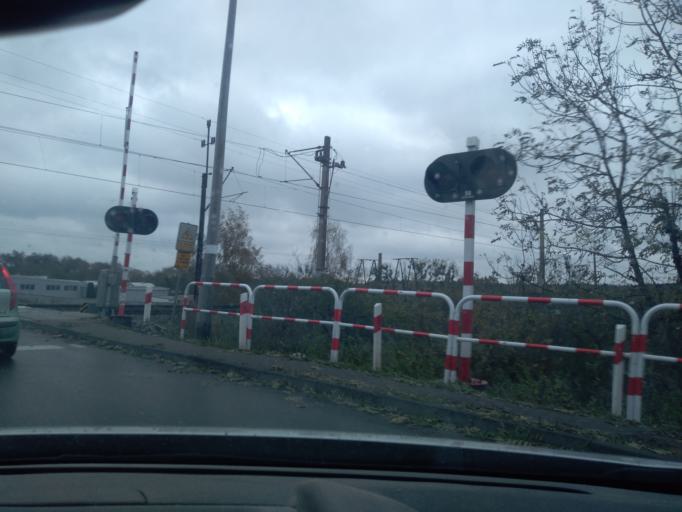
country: PL
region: Greater Poland Voivodeship
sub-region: Powiat obornicki
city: Oborniki
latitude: 52.6443
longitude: 16.8196
